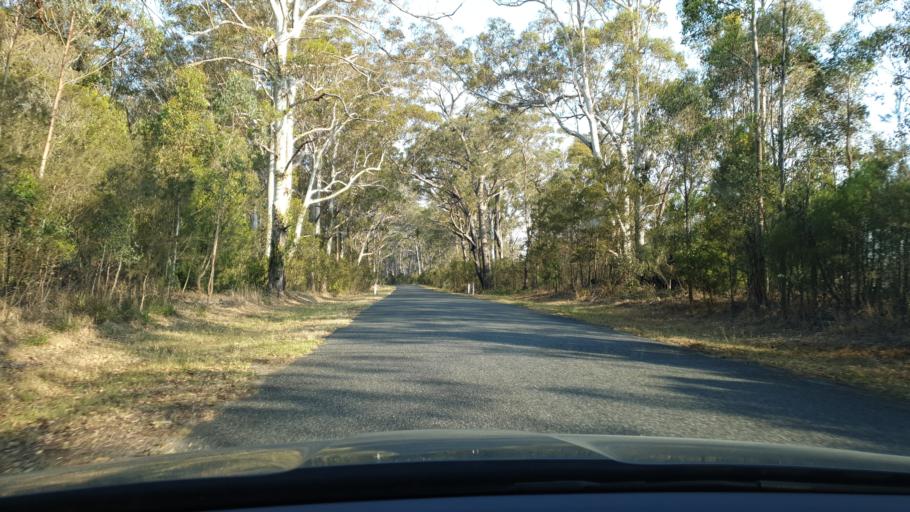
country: AU
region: New South Wales
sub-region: Tenterfield Municipality
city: Carrolls Creek
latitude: -28.6975
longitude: 152.0933
